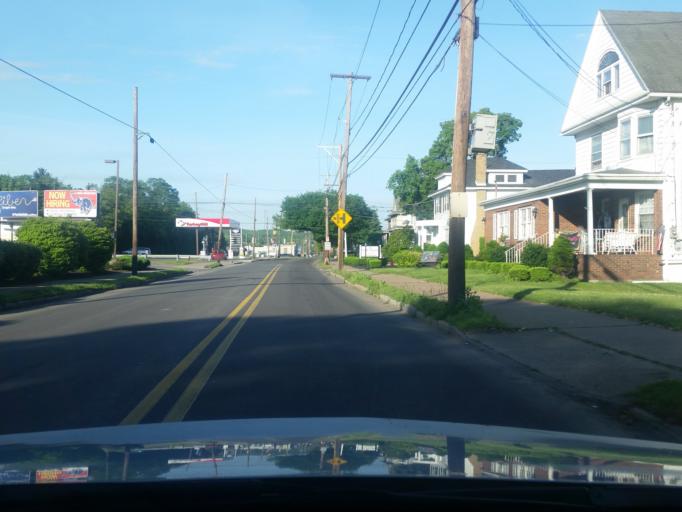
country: US
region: Pennsylvania
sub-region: Luzerne County
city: Larksville
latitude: 41.2359
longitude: -75.9163
